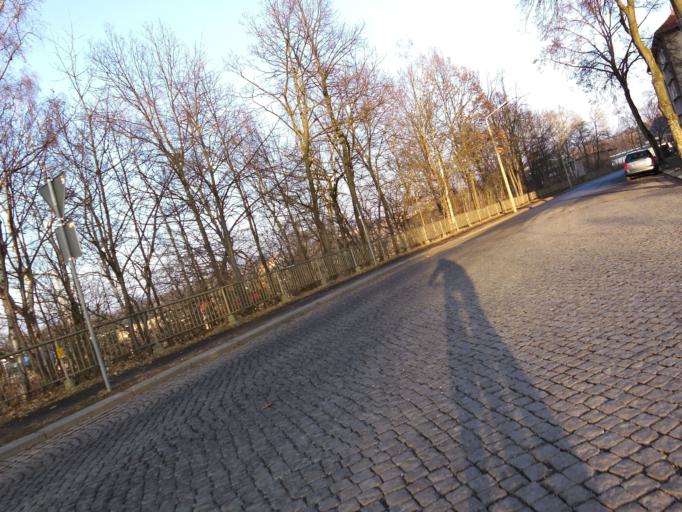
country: DE
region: Saxony
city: Glauchau
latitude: 50.8285
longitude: 12.5518
